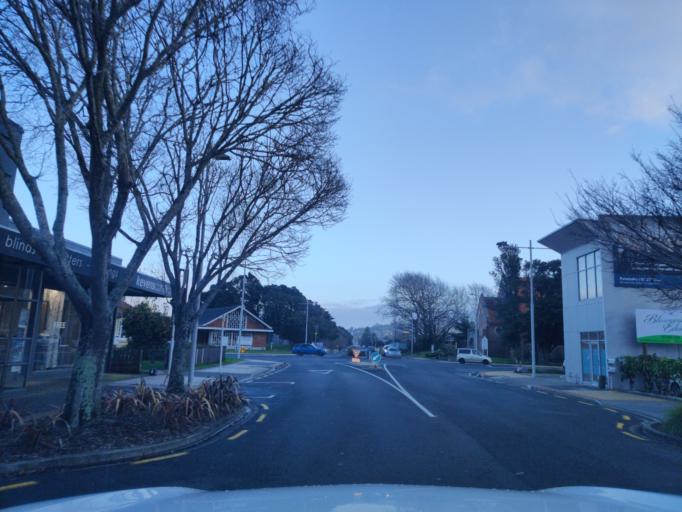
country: NZ
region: Auckland
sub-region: Auckland
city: Pukekohe East
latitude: -37.2013
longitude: 174.9011
